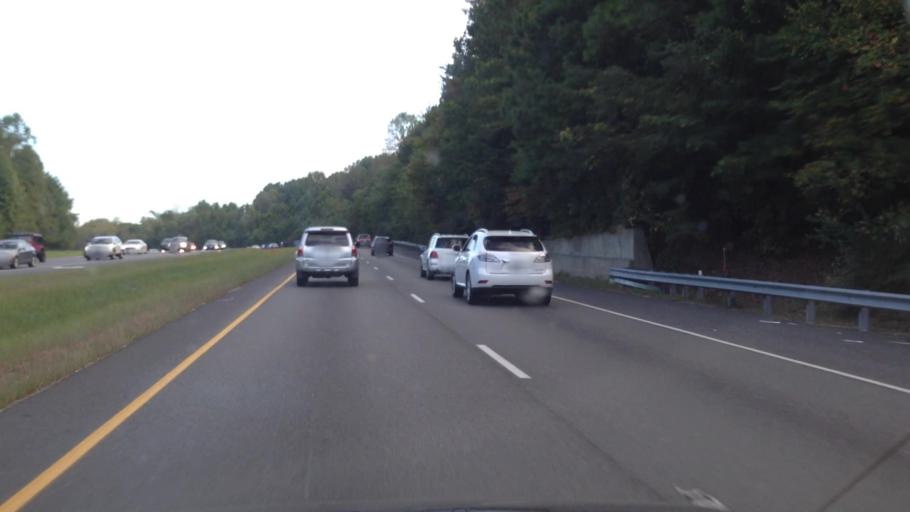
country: US
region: Virginia
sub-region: Fairfax County
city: Fairfax Station
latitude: 38.8107
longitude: -77.3427
